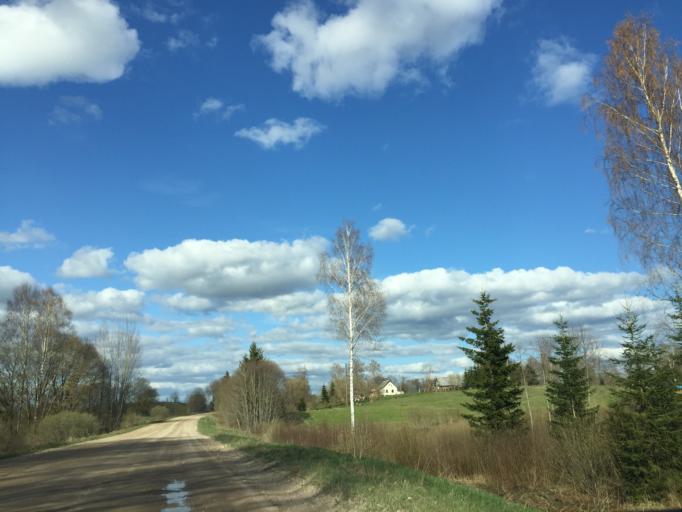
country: LV
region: Rezekne
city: Rezekne
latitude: 56.6371
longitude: 27.3141
